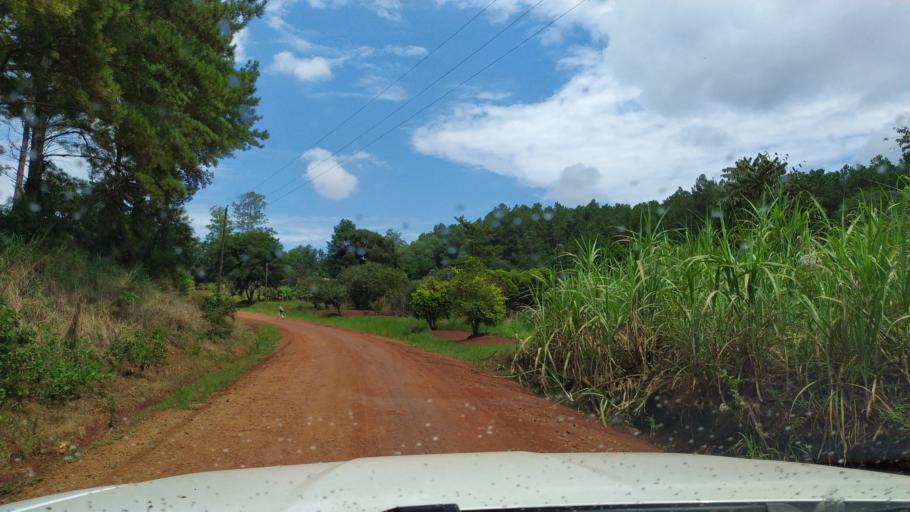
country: AR
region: Misiones
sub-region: Departamento de Eldorado
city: Eldorado
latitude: -26.5004
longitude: -54.5901
